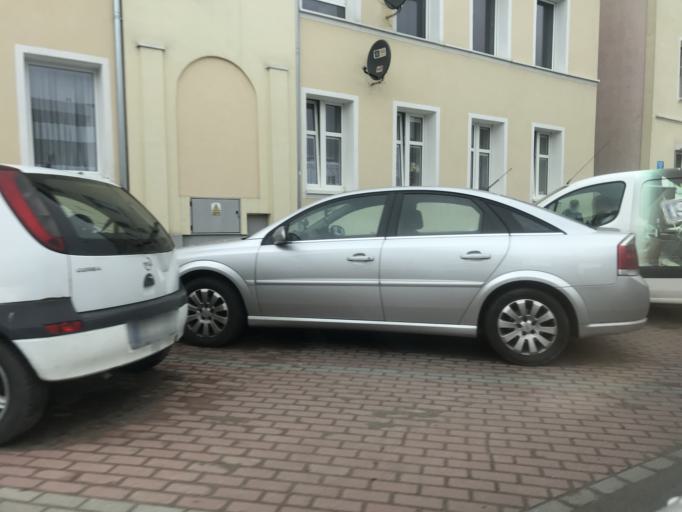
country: PL
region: Warmian-Masurian Voivodeship
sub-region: Powiat elblaski
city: Elblag
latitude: 54.1539
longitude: 19.4193
